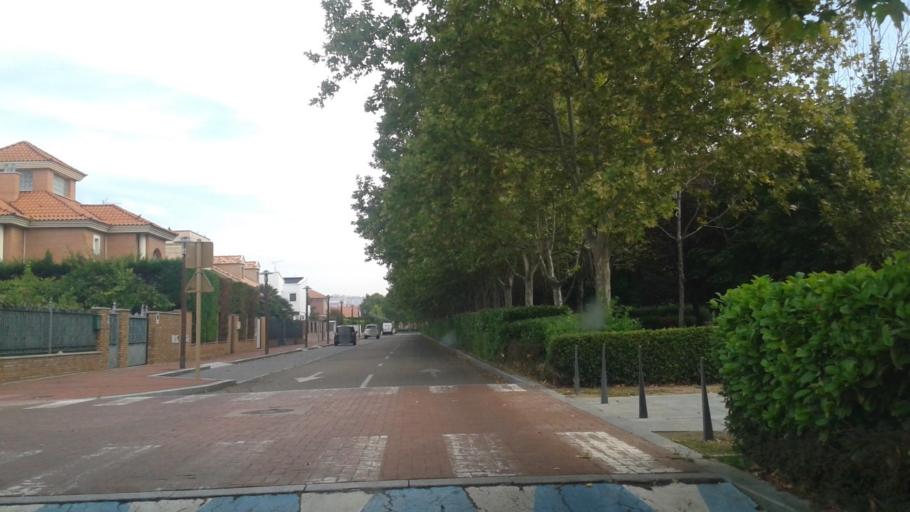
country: ES
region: Castille and Leon
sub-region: Provincia de Valladolid
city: Arroyo
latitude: 41.6141
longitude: -4.7832
